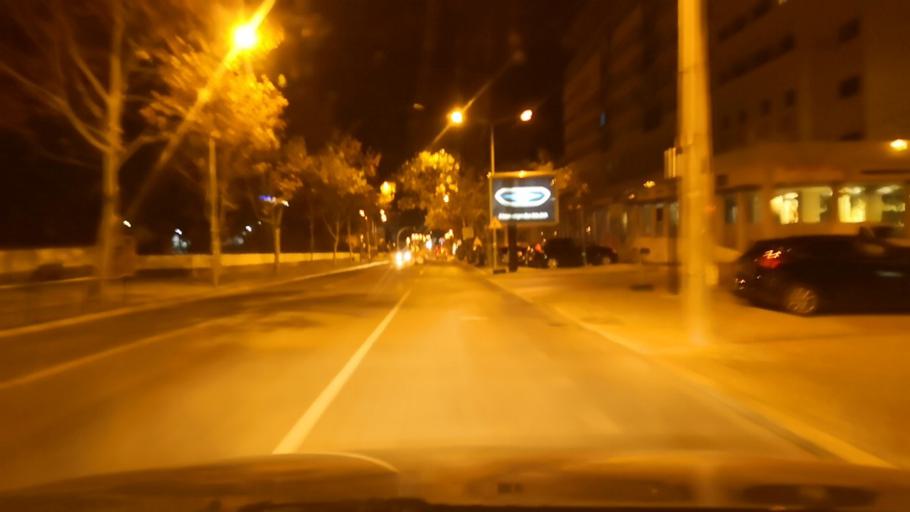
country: PT
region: Setubal
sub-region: Setubal
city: Setubal
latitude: 38.5336
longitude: -8.8930
